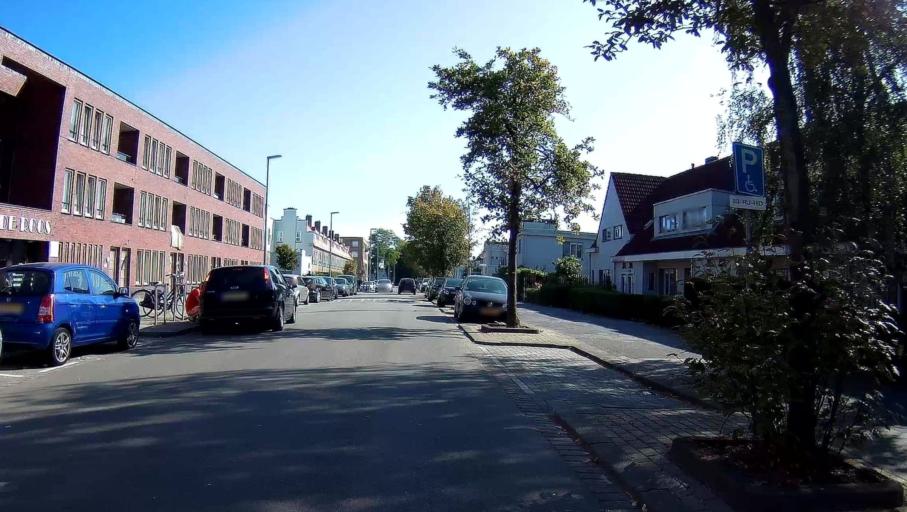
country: NL
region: South Holland
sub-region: Gemeente Rotterdam
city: Rotterdam
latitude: 51.8944
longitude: 4.4991
